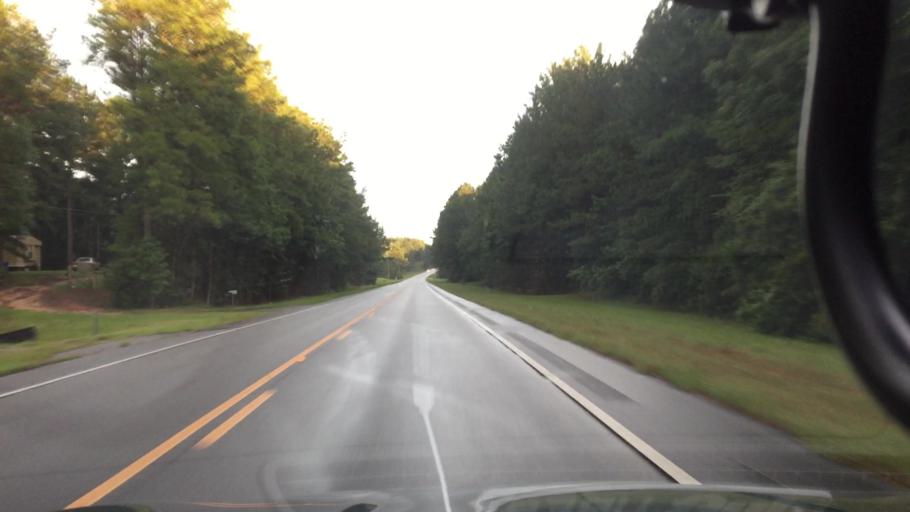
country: US
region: Alabama
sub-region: Coffee County
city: New Brockton
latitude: 31.5584
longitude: -85.9229
